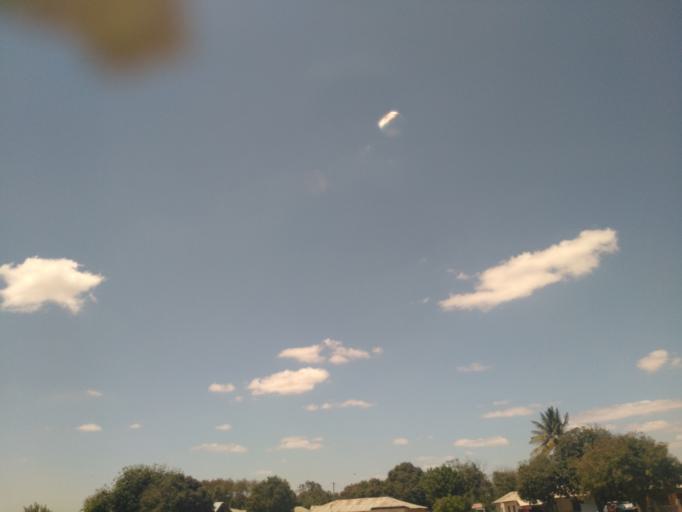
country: TZ
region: Dodoma
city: Dodoma
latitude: -6.1899
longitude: 35.7360
